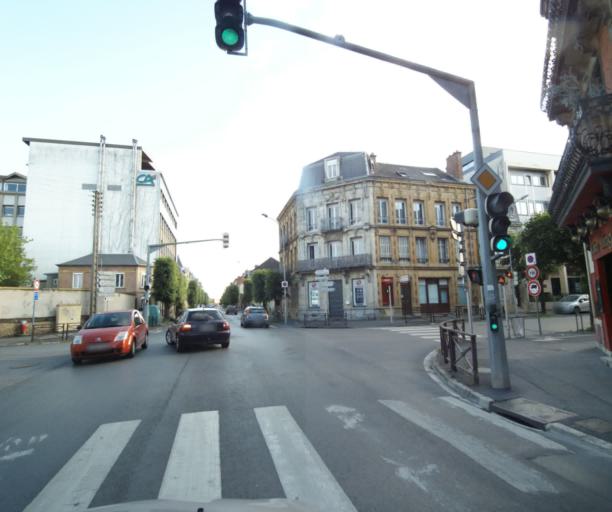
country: FR
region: Champagne-Ardenne
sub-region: Departement des Ardennes
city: Charleville-Mezieres
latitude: 49.7725
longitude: 4.7260
